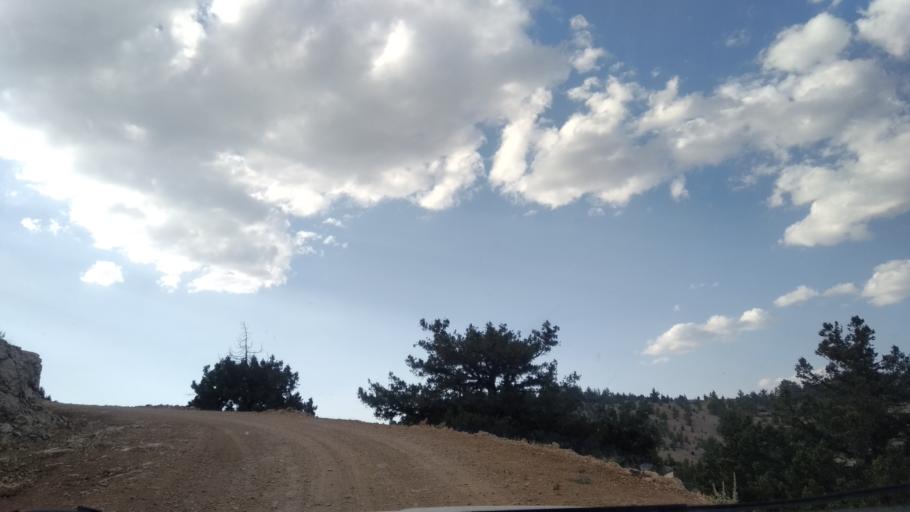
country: TR
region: Mersin
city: Sarikavak
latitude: 36.5995
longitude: 33.7028
